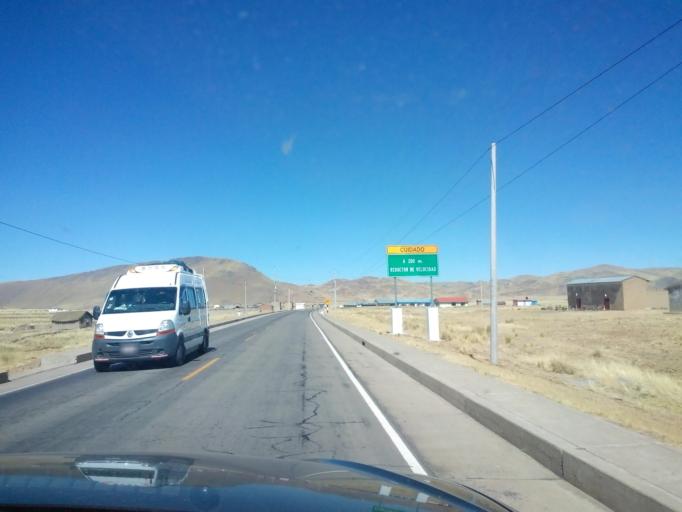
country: PE
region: Puno
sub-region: Provincia de Melgar
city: Santa Rosa
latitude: -14.5661
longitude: -70.8749
